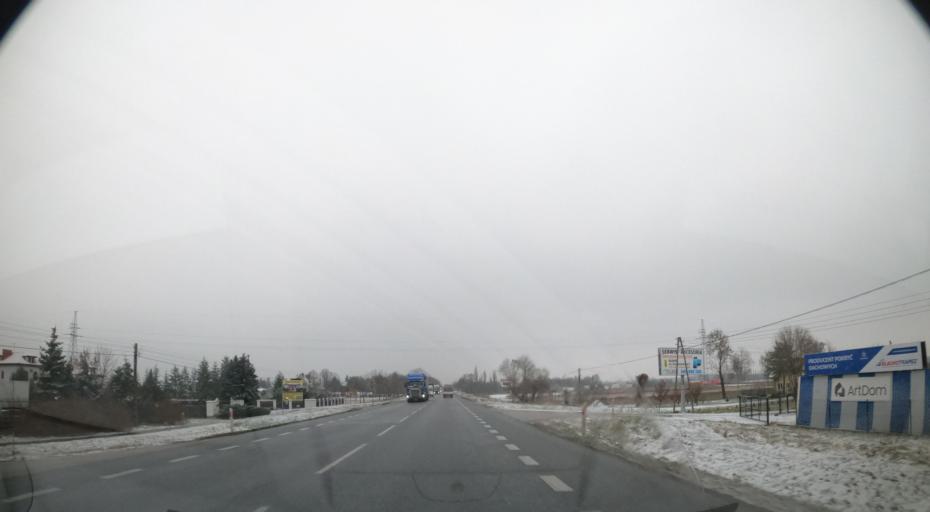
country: PL
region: Masovian Voivodeship
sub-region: Powiat warszawski zachodni
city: Bieniewice
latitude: 52.1999
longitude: 20.5842
